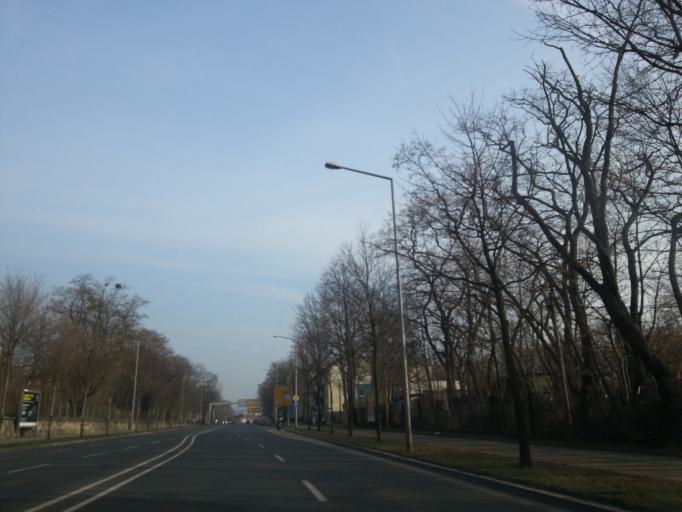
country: DE
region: Saxony
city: Albertstadt
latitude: 51.0728
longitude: 13.7667
